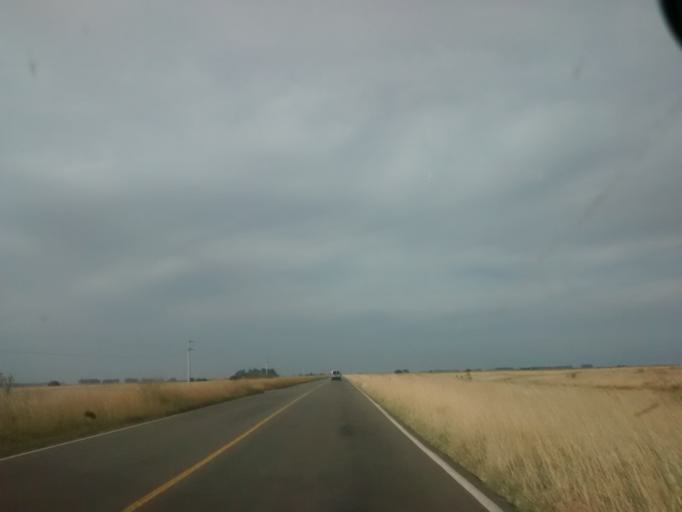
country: AR
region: Buenos Aires
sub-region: Partido de Ayacucho
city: Ayacucho
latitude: -36.8187
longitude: -58.5668
